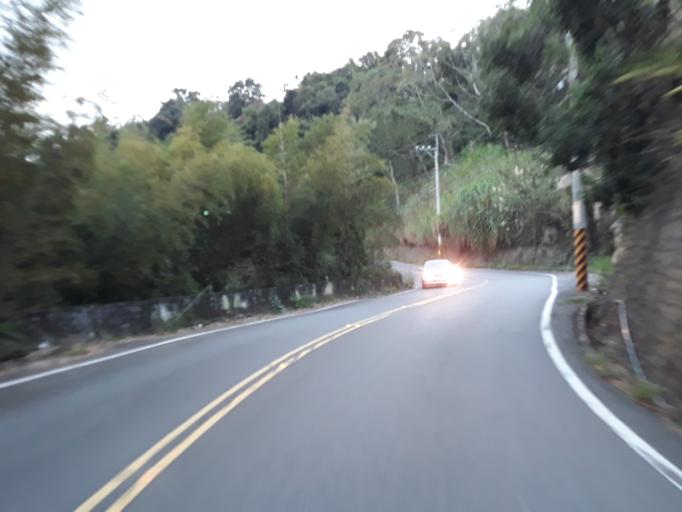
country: TW
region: Taiwan
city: Fengyuan
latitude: 24.3667
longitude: 120.8673
